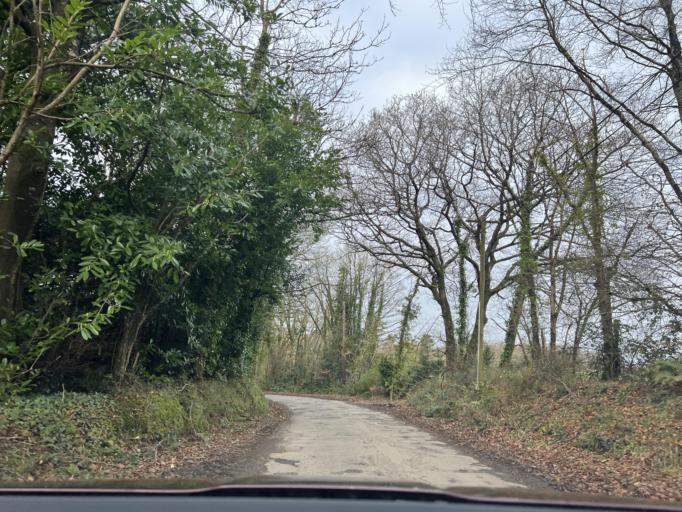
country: IE
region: Leinster
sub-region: Loch Garman
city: Loch Garman
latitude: 52.3722
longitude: -6.5382
